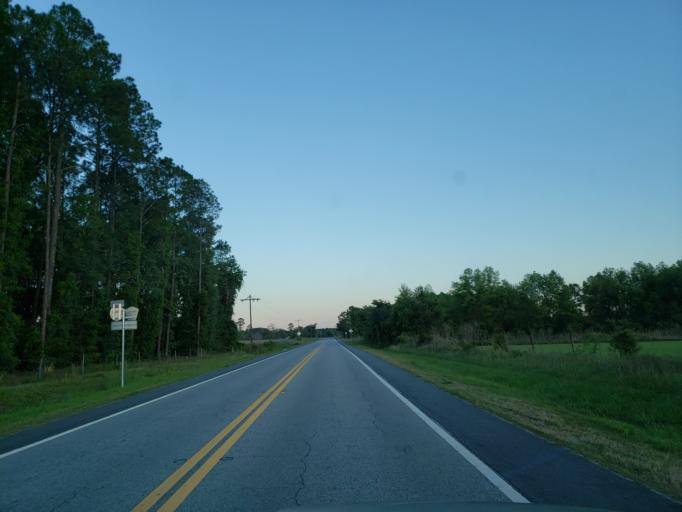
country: US
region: Georgia
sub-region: Echols County
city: Statenville
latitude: 30.5689
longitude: -83.1593
